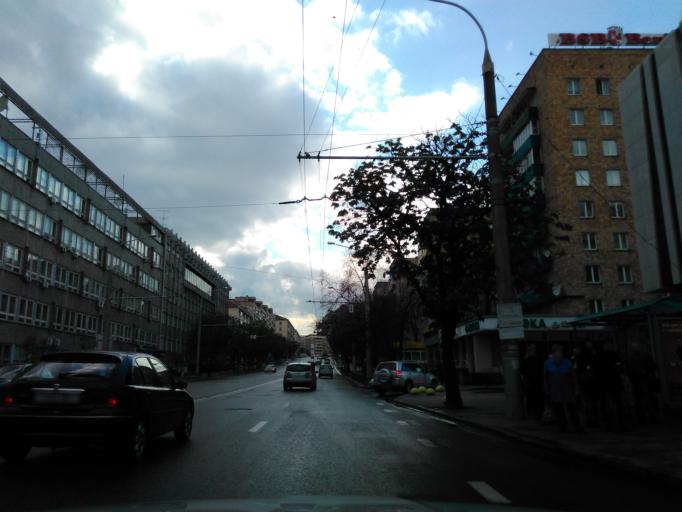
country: BY
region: Minsk
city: Minsk
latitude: 53.9025
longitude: 27.5473
